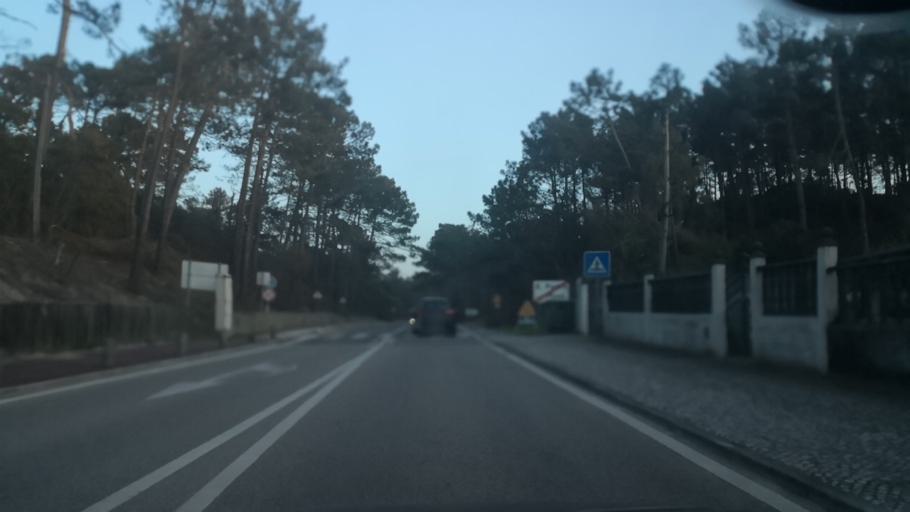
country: PT
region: Leiria
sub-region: Alcobaca
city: Pataias
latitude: 39.7547
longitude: -9.0246
